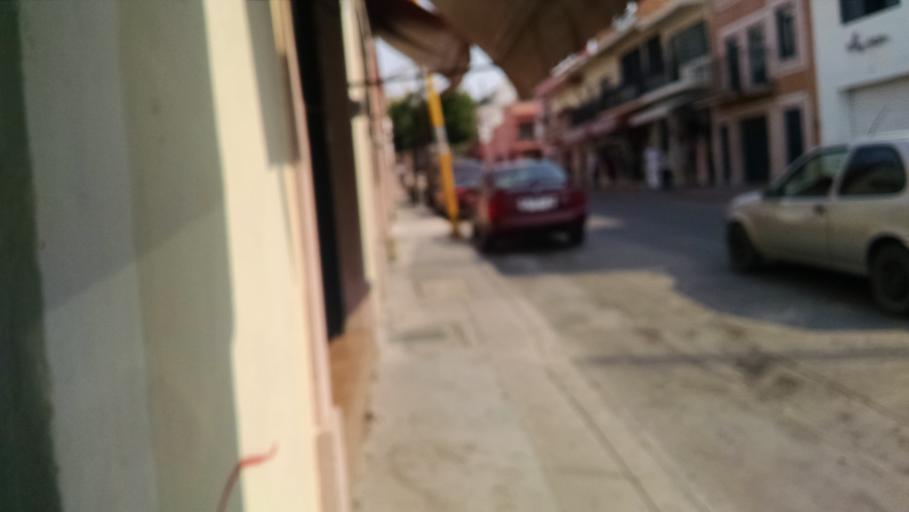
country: MX
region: Aguascalientes
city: Calvillo
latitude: 21.8470
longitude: -102.7164
